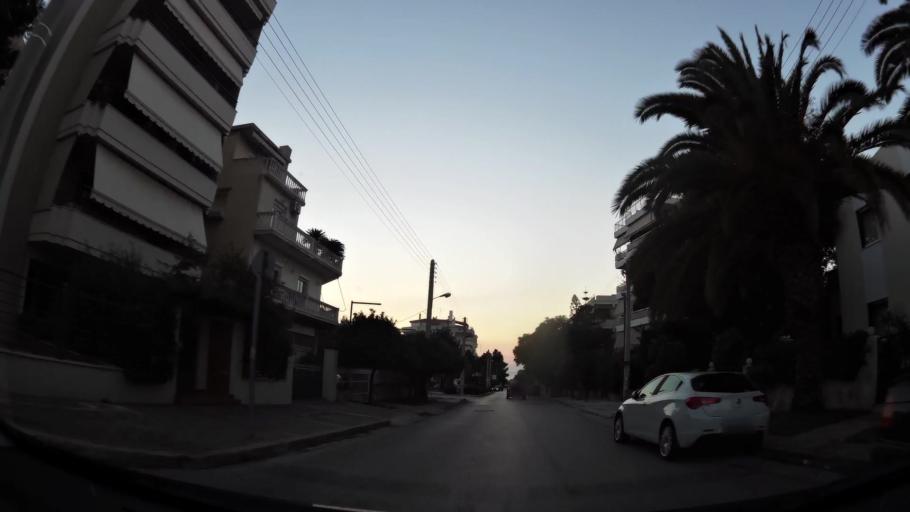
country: GR
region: Attica
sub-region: Nomarchia Athinas
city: Argyroupoli
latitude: 37.8893
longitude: 23.7575
